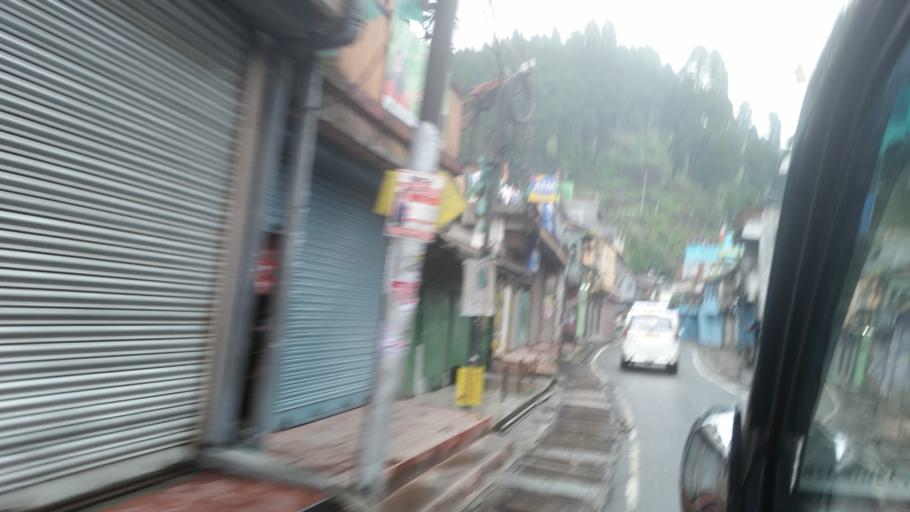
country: IN
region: West Bengal
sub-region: Darjiling
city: Darjiling
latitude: 27.0083
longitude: 88.2594
